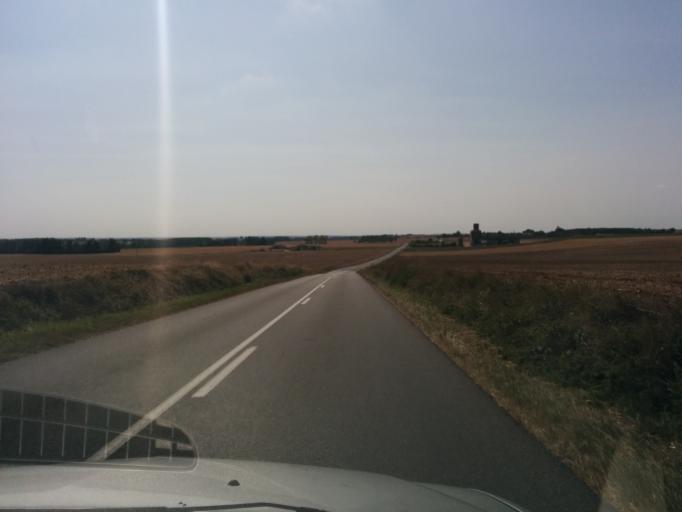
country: FR
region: Poitou-Charentes
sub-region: Departement de la Vienne
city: Saint-Jean-de-Sauves
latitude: 46.8000
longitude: 0.0979
